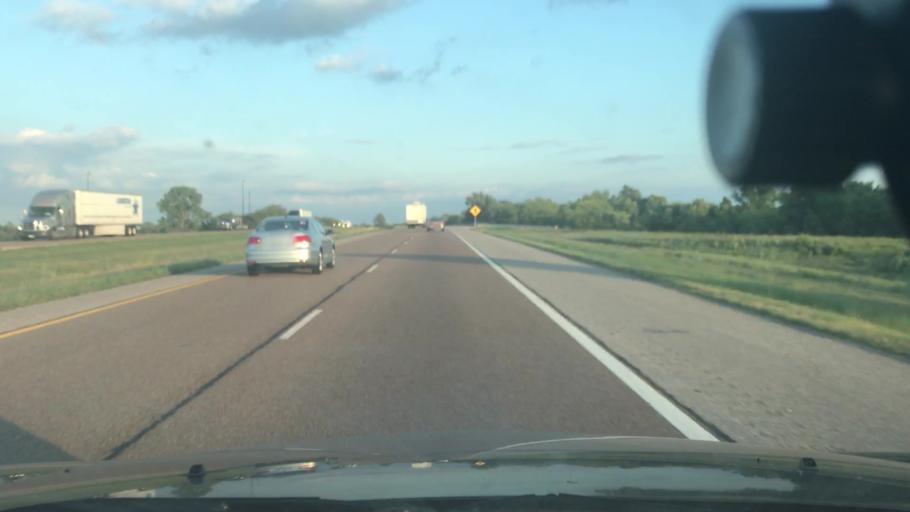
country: US
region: Illinois
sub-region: Clinton County
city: New Baden
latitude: 38.5343
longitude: -89.7281
